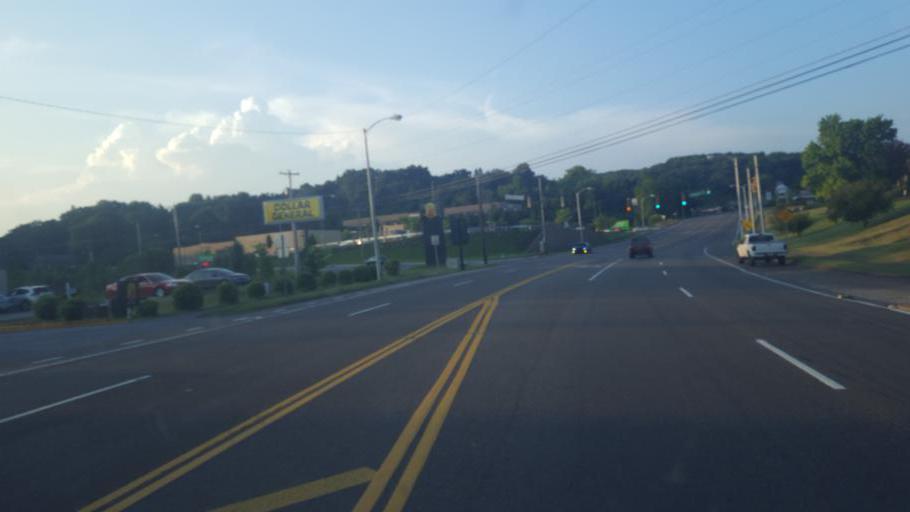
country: US
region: Tennessee
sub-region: Sullivan County
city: Kingsport
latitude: 36.5609
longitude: -82.5678
